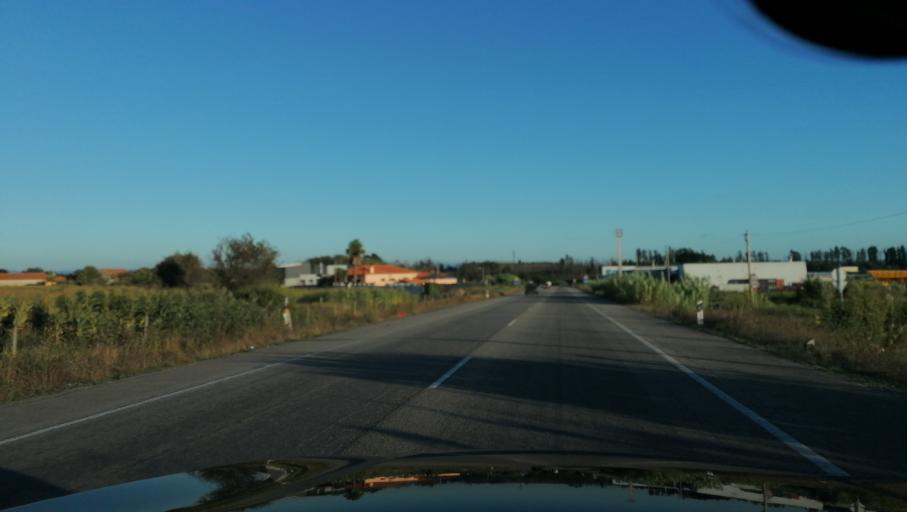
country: PT
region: Aveiro
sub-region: Aveiro
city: Oliveirinha
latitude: 40.5879
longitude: -8.6078
